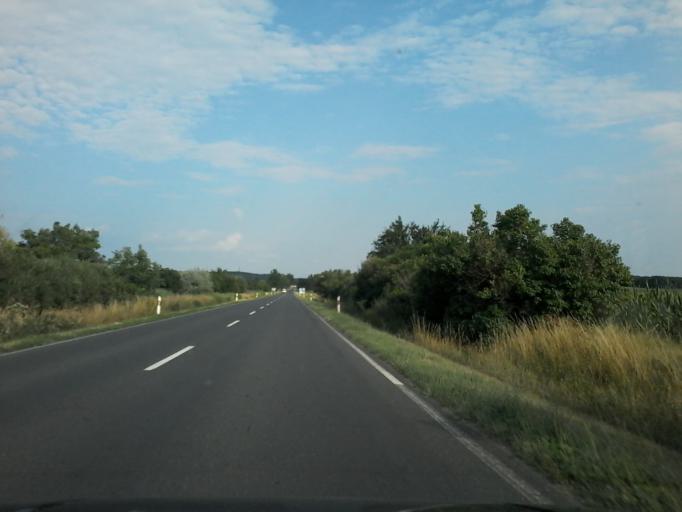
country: HU
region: Vas
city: Janoshaza
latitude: 47.1599
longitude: 17.0620
